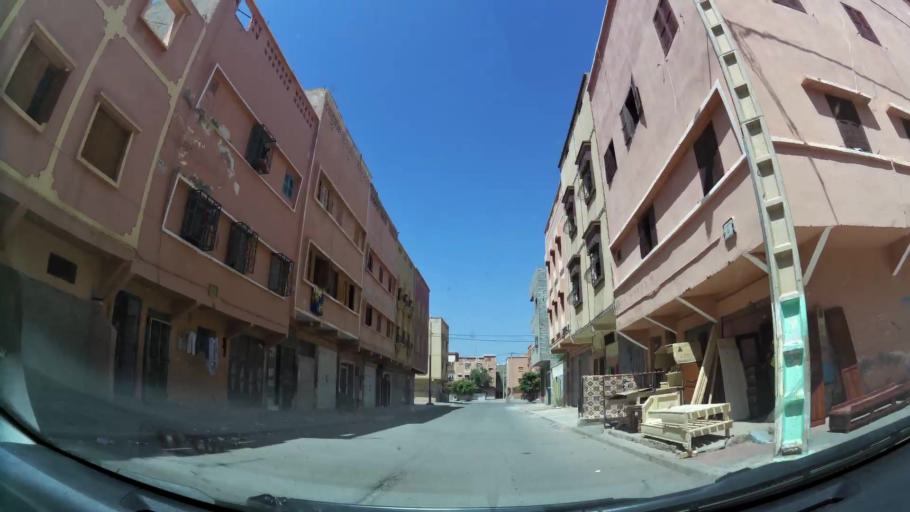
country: MA
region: Souss-Massa-Draa
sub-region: Inezgane-Ait Mellou
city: Inezgane
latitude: 30.3452
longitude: -9.4855
